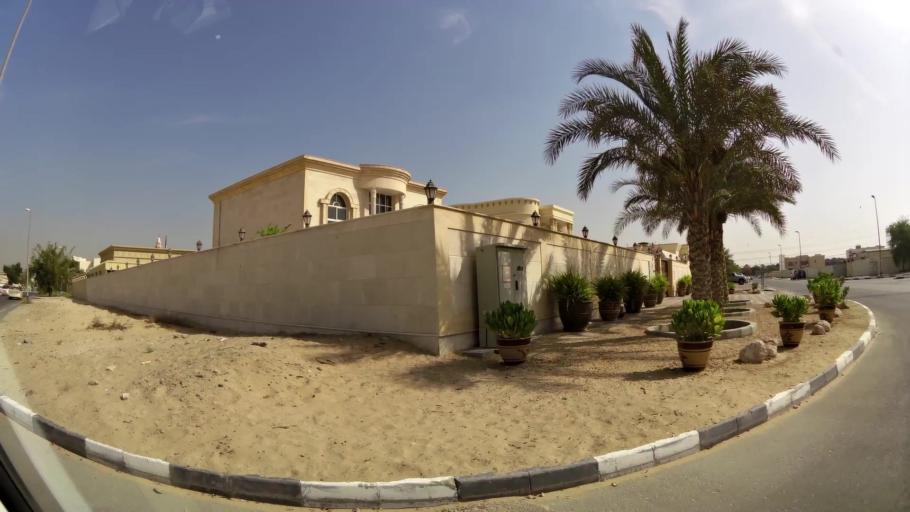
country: AE
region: Ash Shariqah
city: Sharjah
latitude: 25.2654
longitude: 55.3958
